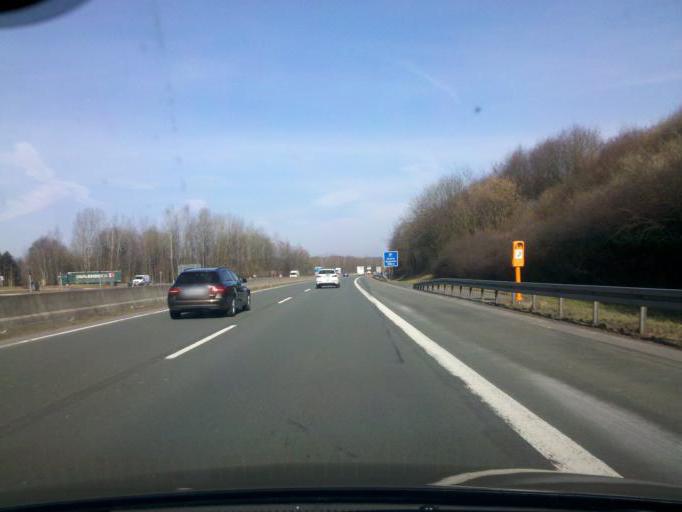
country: DE
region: North Rhine-Westphalia
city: Freudenberg
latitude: 50.9331
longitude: 7.8845
